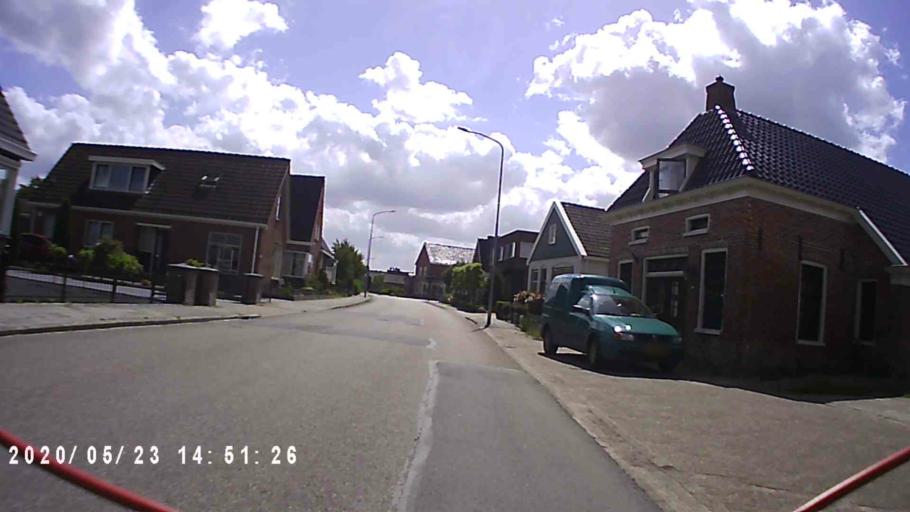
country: NL
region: Groningen
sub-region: Gemeente Delfzijl
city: Delfzijl
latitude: 53.2567
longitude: 6.9338
